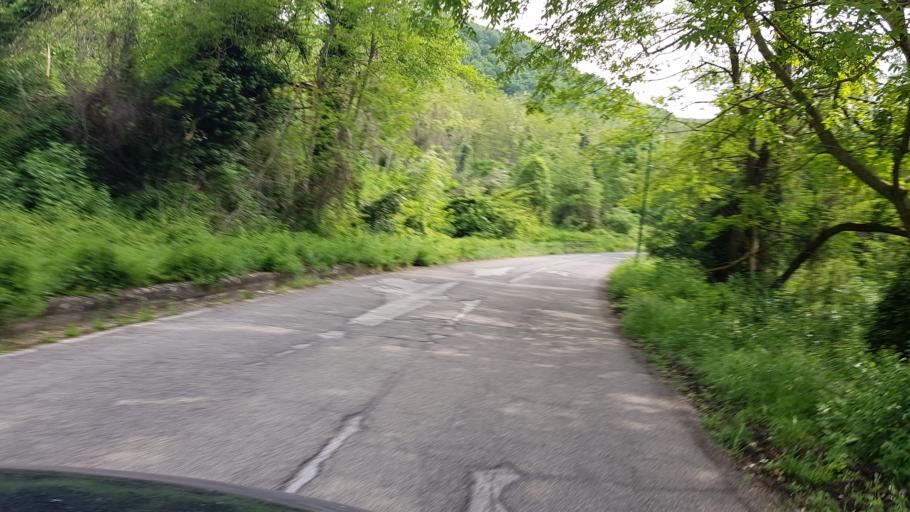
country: IT
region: Basilicate
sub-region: Provincia di Potenza
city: Zona 179
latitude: 40.9363
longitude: 15.6030
